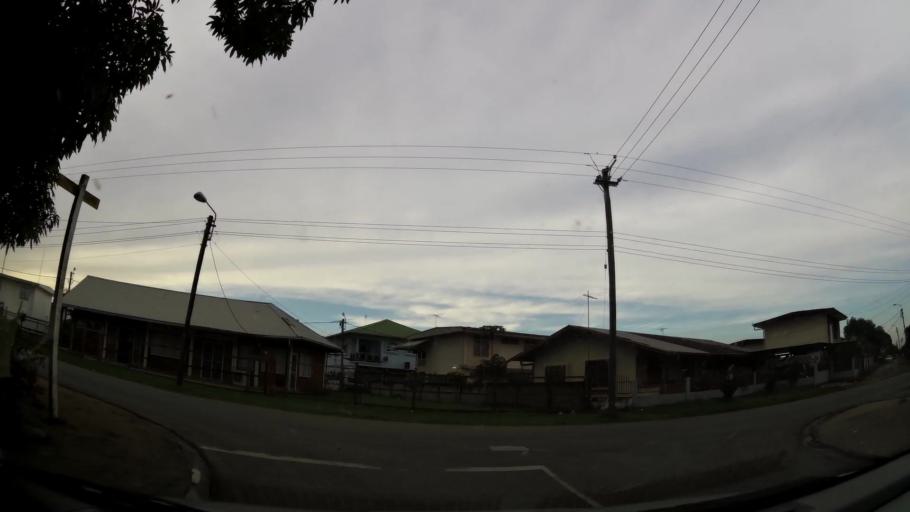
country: SR
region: Paramaribo
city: Paramaribo
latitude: 5.8128
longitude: -55.2041
